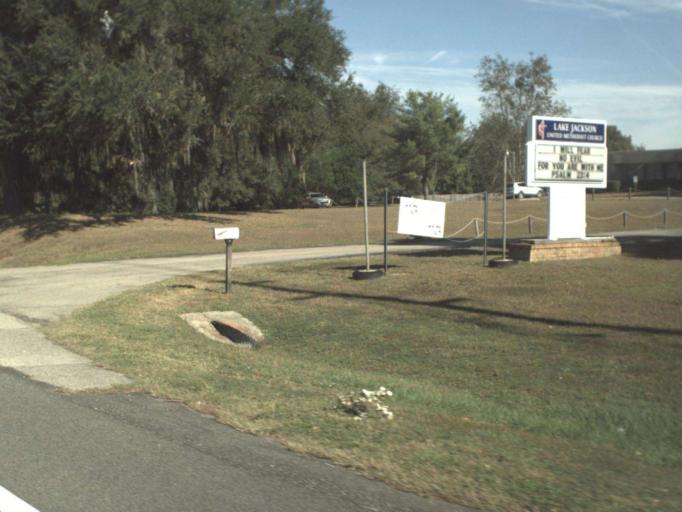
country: US
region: Florida
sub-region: Leon County
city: Tallahassee
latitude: 30.5154
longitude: -84.3459
